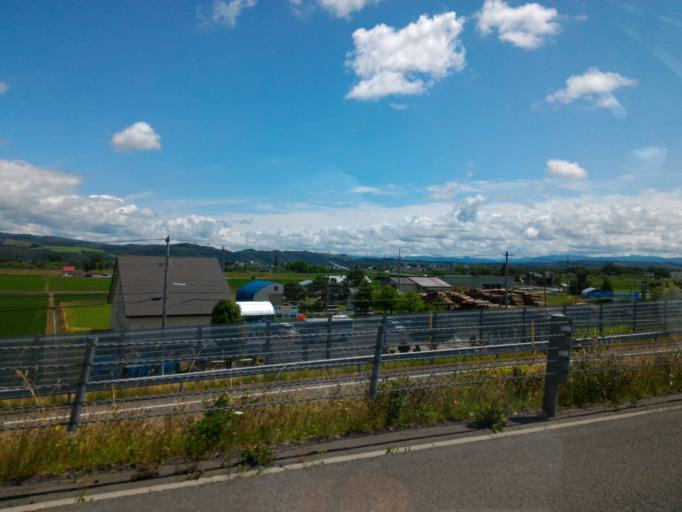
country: JP
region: Hokkaido
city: Nayoro
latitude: 44.3634
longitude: 142.4358
